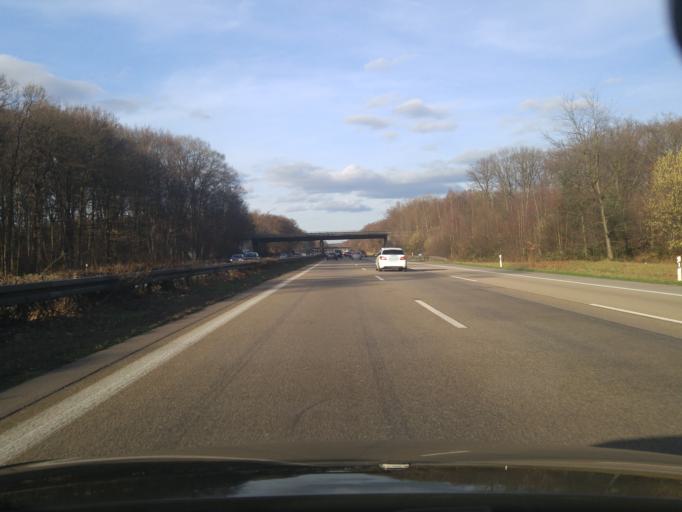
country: DE
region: North Rhine-Westphalia
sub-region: Regierungsbezirk Dusseldorf
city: Langenfeld
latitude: 51.1365
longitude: 6.9722
